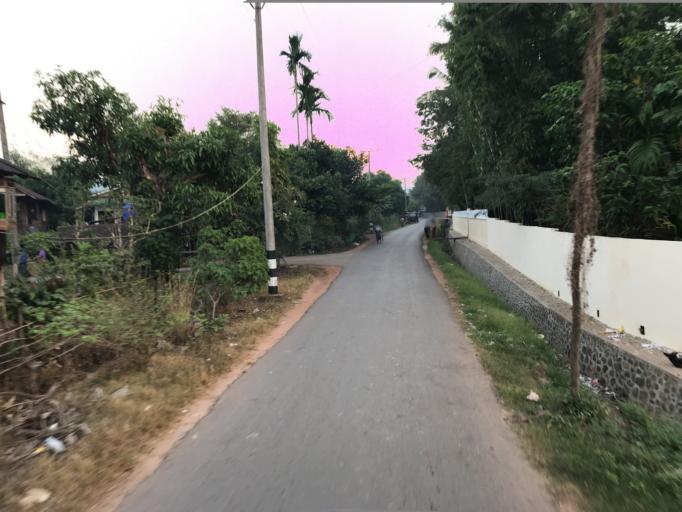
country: MM
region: Mon
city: Kyaikkami
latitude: 15.9628
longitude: 97.7316
